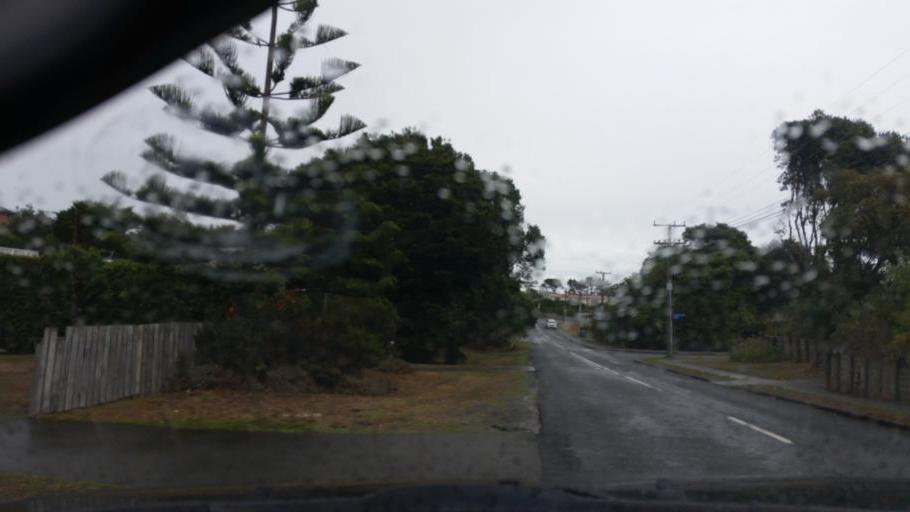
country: NZ
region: Auckland
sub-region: Auckland
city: Wellsford
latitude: -36.0937
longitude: 174.5901
